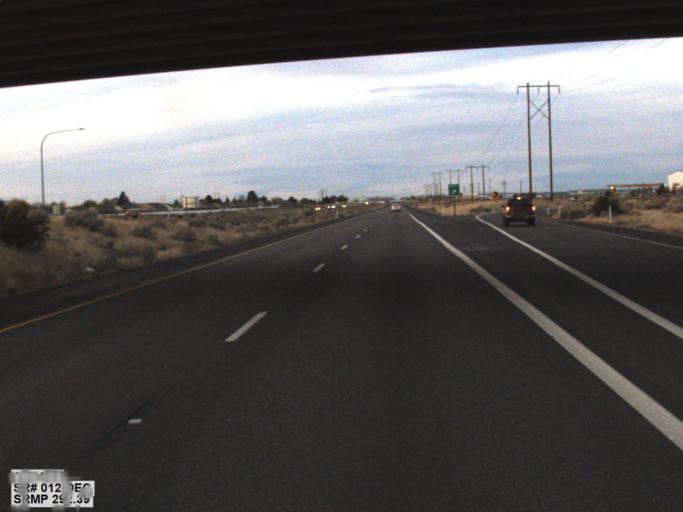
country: US
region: Washington
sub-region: Franklin County
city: Pasco
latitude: 46.2395
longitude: -119.0567
